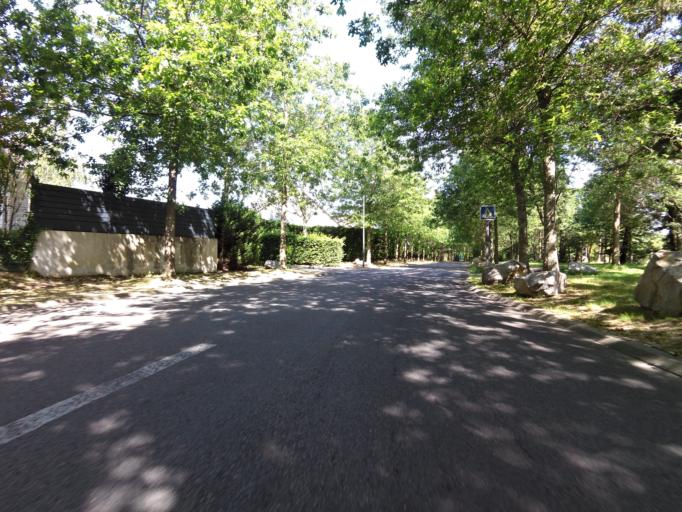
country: FR
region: Pays de la Loire
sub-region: Departement de la Loire-Atlantique
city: Saint-Herblain
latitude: 47.2278
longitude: -1.6127
